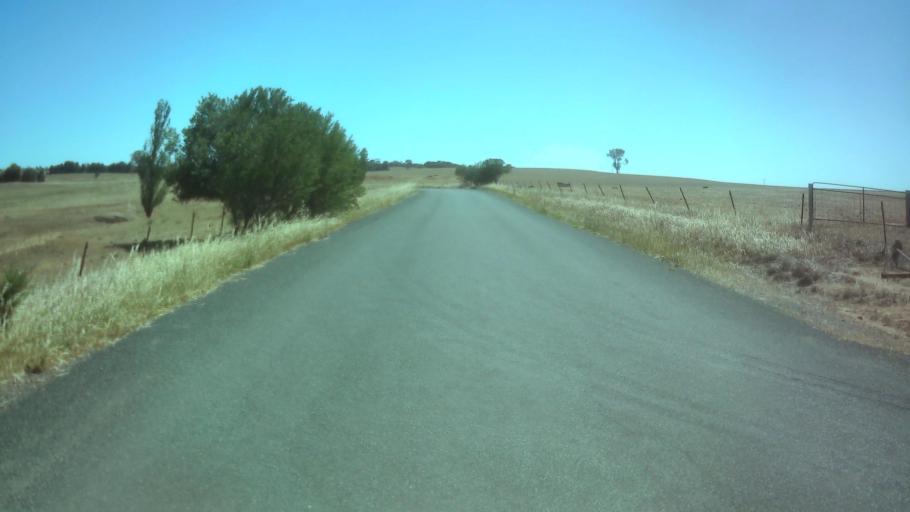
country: AU
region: New South Wales
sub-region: Weddin
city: Grenfell
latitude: -33.9773
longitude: 148.4021
